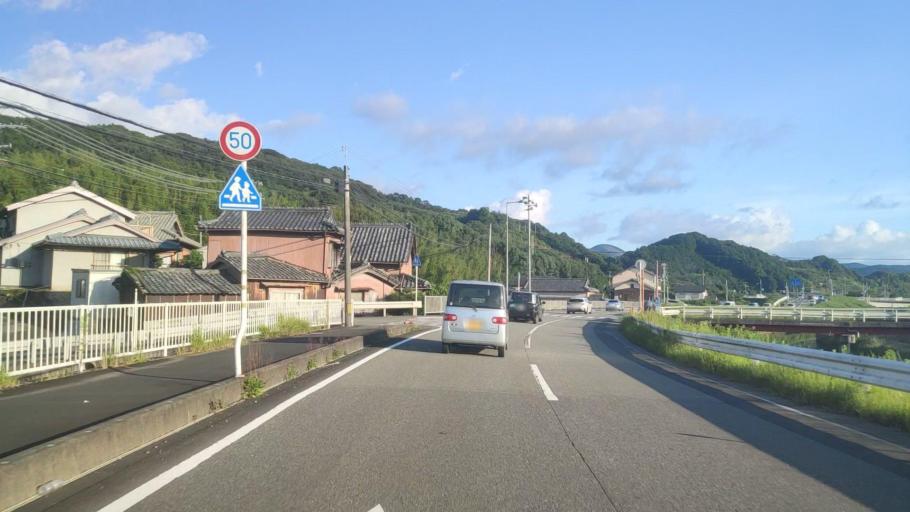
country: JP
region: Wakayama
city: Tanabe
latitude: 33.7160
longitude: 135.4478
